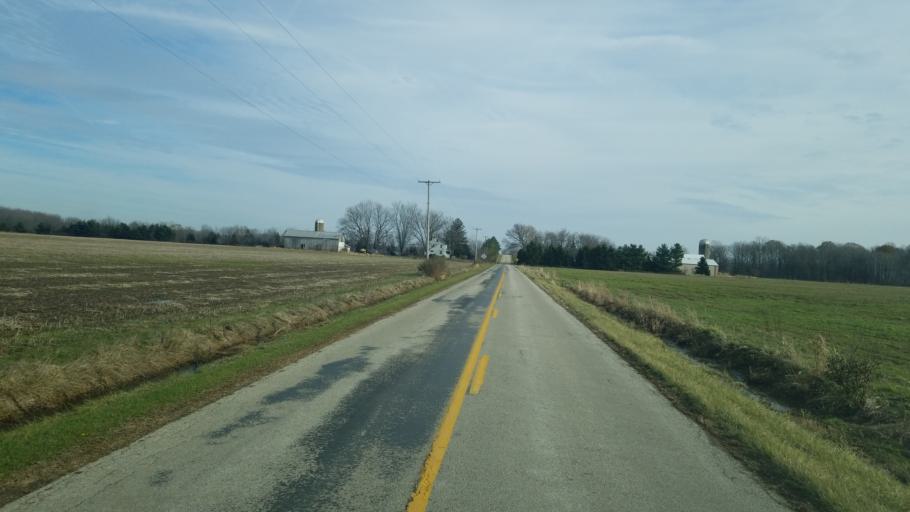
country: US
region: Ohio
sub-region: Ashtabula County
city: Roaming Shores
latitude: 41.6351
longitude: -80.7209
